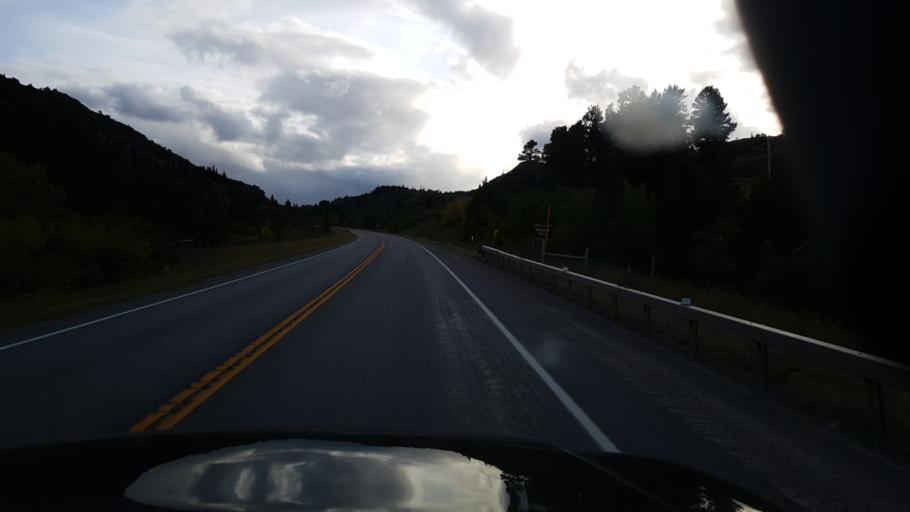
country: US
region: Montana
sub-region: Glacier County
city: South Browning
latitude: 48.4023
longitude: -113.2493
